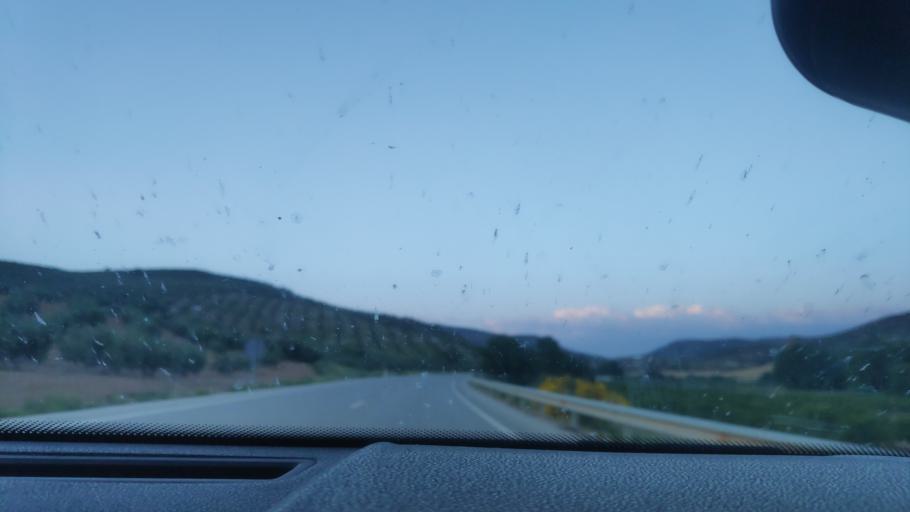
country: ES
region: Andalusia
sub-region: Provincia de Granada
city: Benalua de las Villas
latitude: 37.4459
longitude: -3.6491
